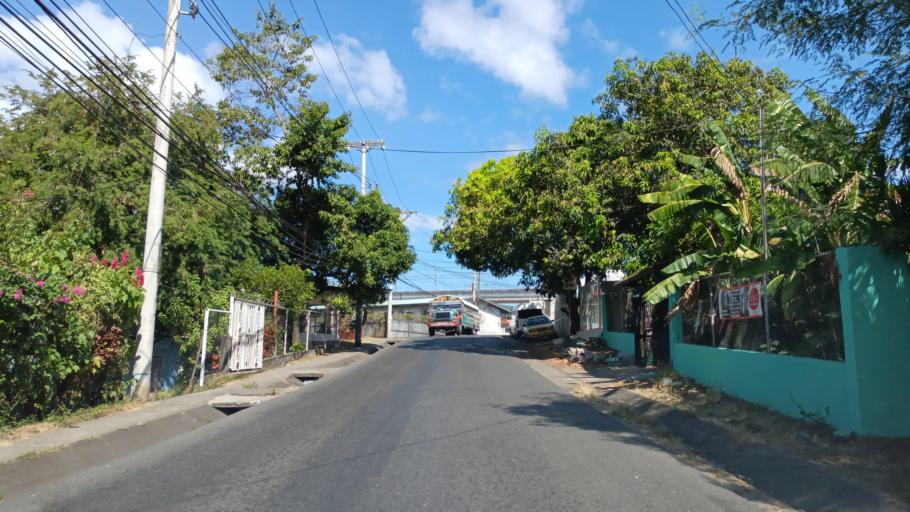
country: PA
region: Panama
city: Tocumen
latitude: 9.1024
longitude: -79.3715
